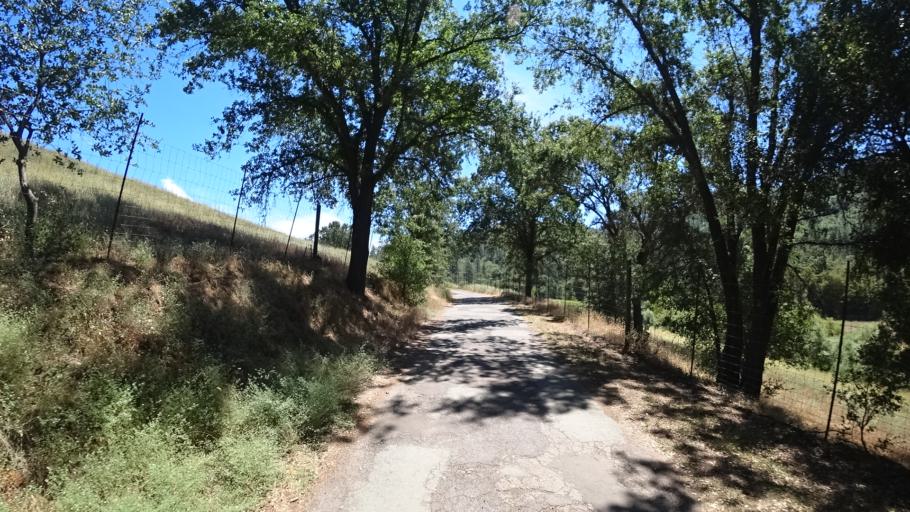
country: US
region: California
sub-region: Calaveras County
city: Murphys
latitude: 38.1547
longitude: -120.4869
